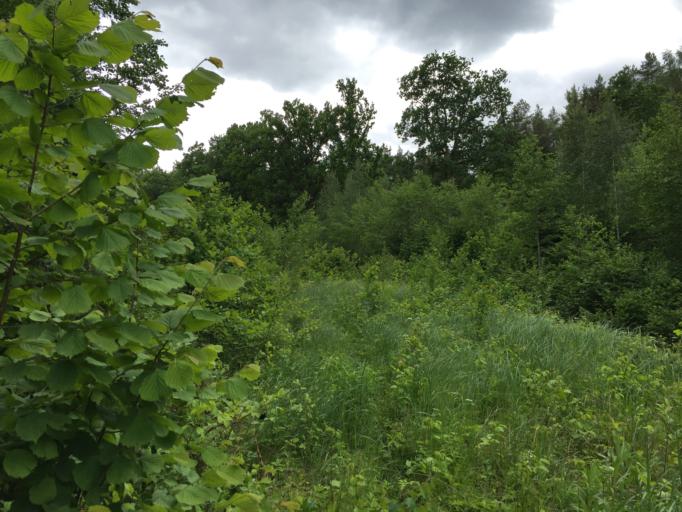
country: LV
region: Lecava
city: Iecava
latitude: 56.5775
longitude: 24.2710
